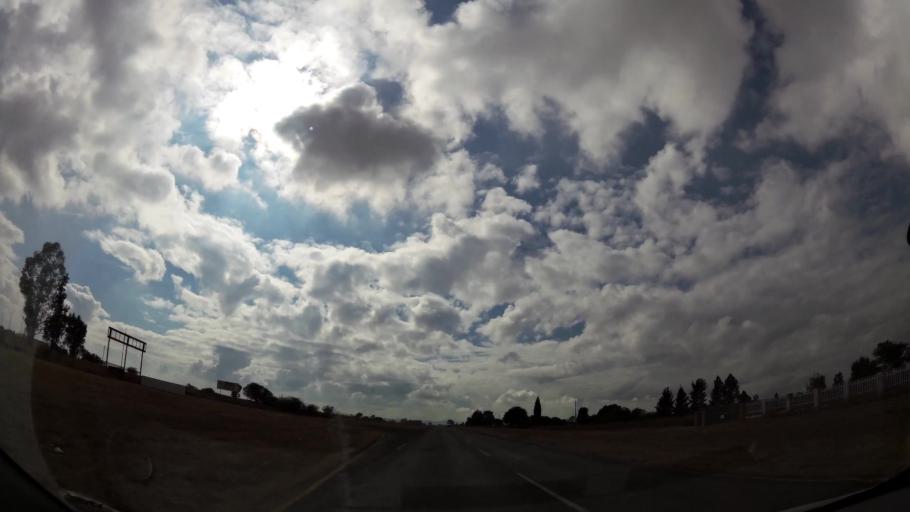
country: ZA
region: Gauteng
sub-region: Sedibeng District Municipality
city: Meyerton
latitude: -26.6162
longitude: 28.0614
